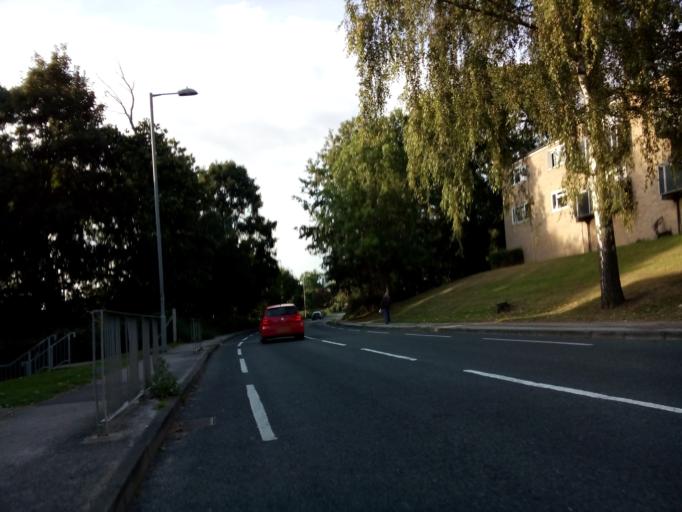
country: GB
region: England
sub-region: Suffolk
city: Ipswich
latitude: 52.0326
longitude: 1.1278
